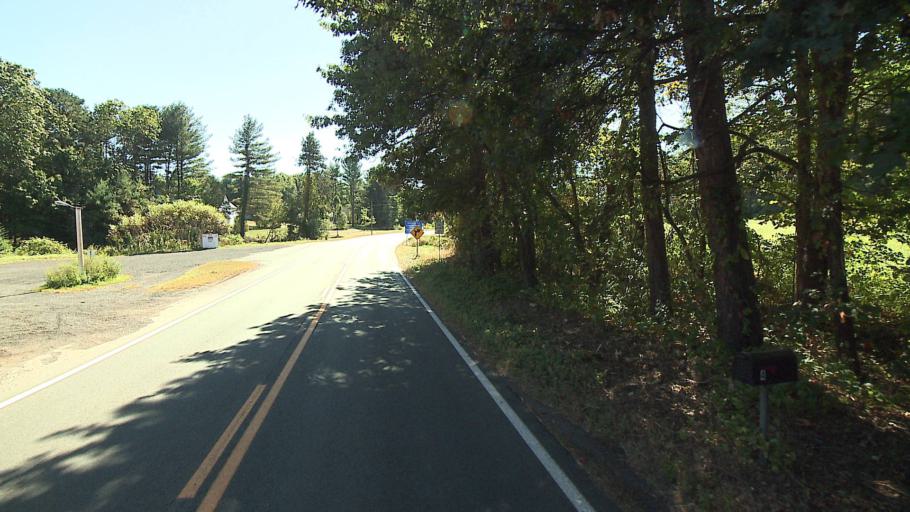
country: US
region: Connecticut
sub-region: Hartford County
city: North Granby
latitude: 42.0004
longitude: -72.7949
